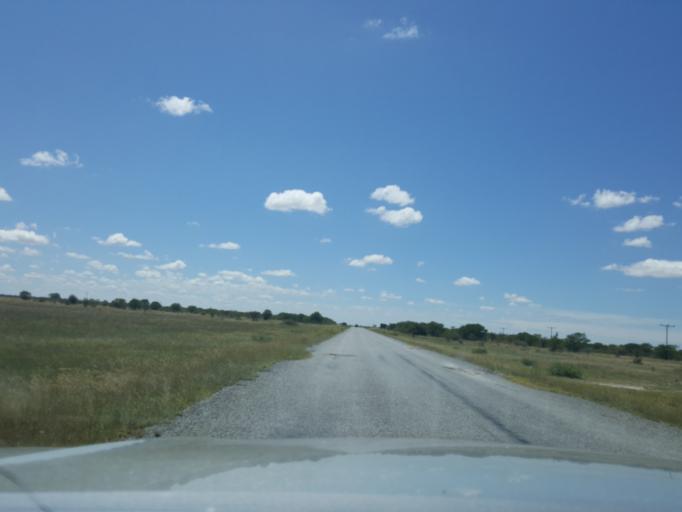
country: BW
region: Central
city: Gweta
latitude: -20.1404
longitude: 25.5233
